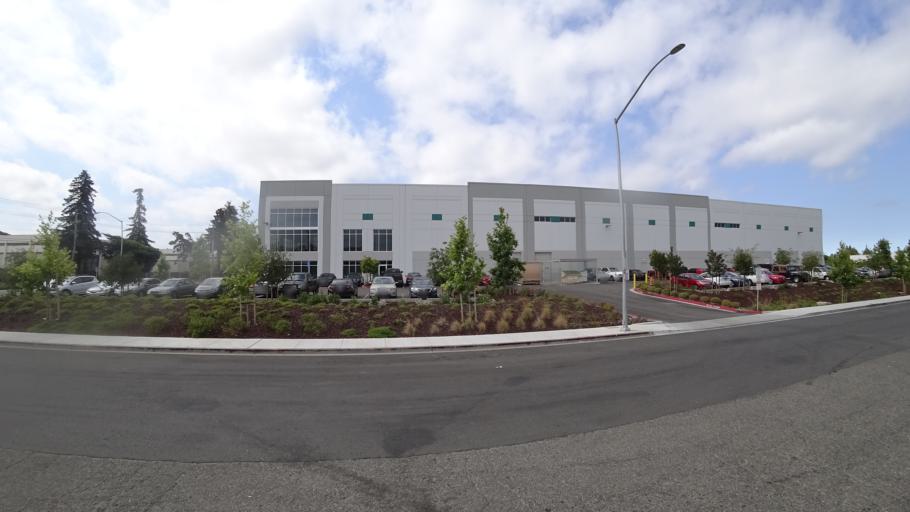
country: US
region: California
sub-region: Alameda County
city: Union City
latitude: 37.6115
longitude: -122.0455
